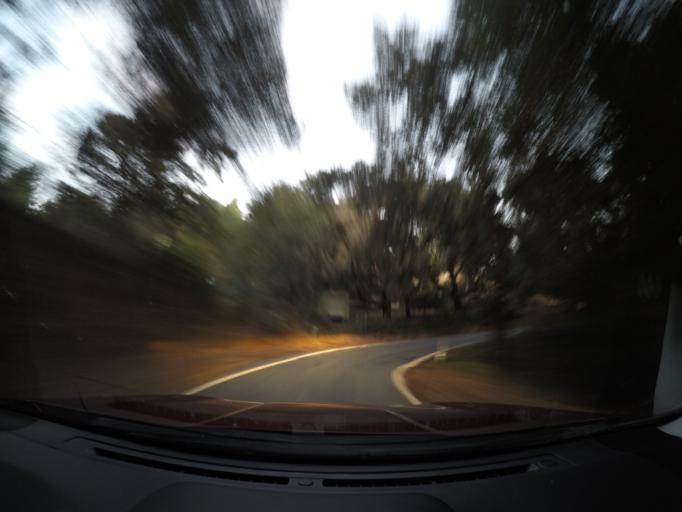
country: US
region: California
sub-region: Santa Clara County
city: Lexington Hills
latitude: 37.1598
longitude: -122.0084
